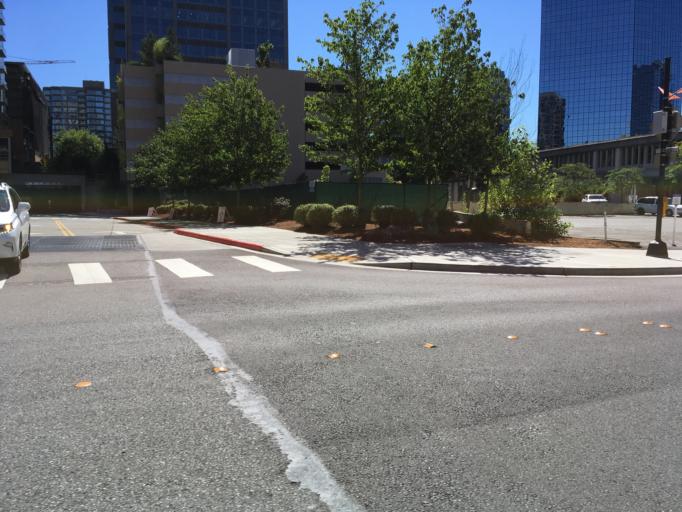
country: US
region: Washington
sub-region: King County
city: Bellevue
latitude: 47.6185
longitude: -122.1991
